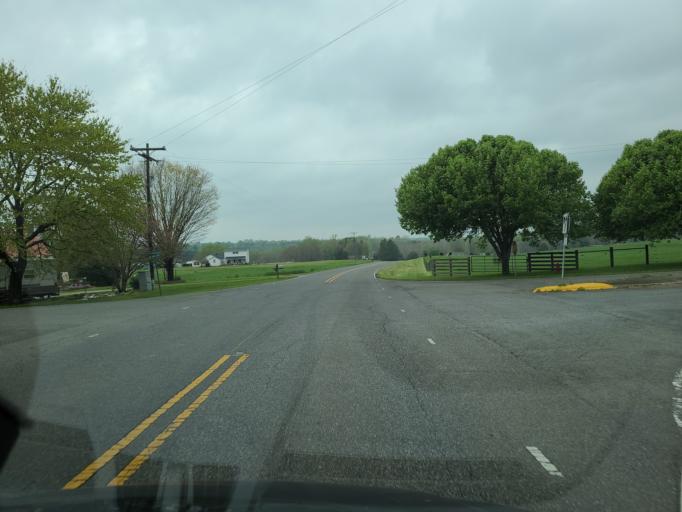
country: US
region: North Carolina
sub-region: Gaston County
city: Cherryville
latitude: 35.4284
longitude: -81.4674
